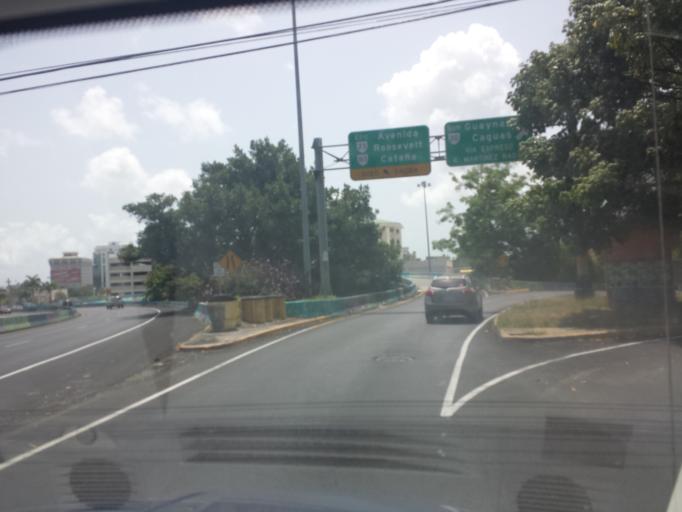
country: PR
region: Catano
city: Catano
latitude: 18.4072
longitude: -66.1091
